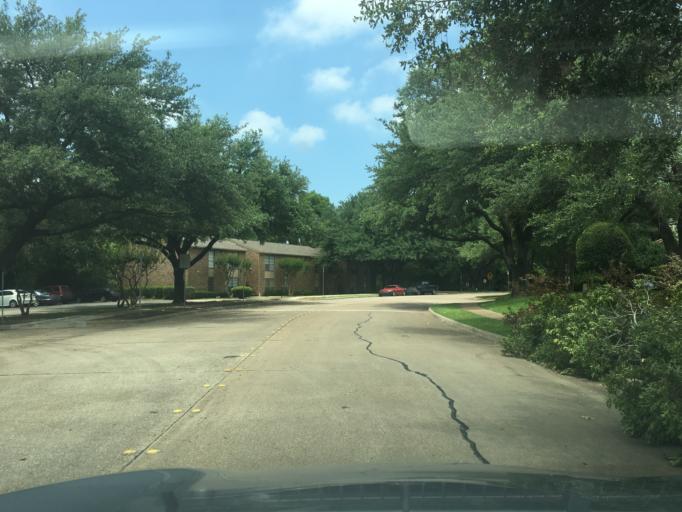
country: US
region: Texas
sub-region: Dallas County
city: Richardson
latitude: 32.9442
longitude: -96.7632
